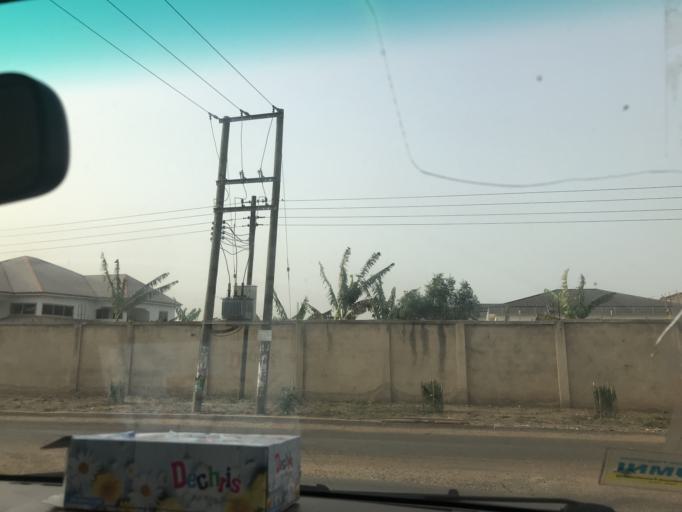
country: GH
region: Greater Accra
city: Nungua
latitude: 5.6369
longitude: -0.0772
